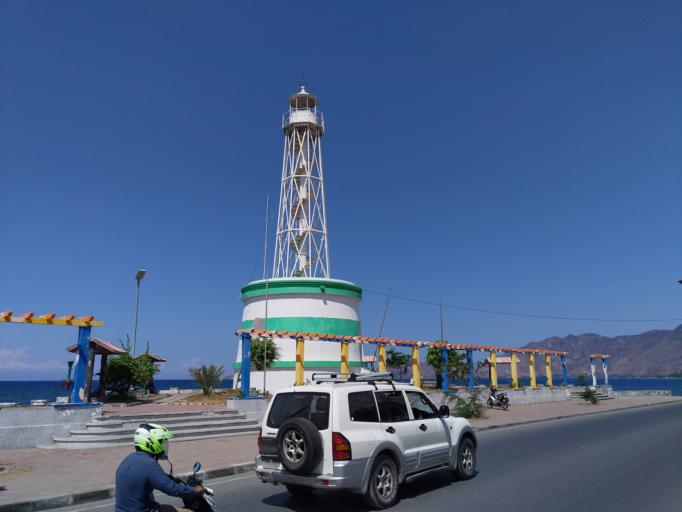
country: TL
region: Dili
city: Dili
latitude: -8.5485
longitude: 125.5685
